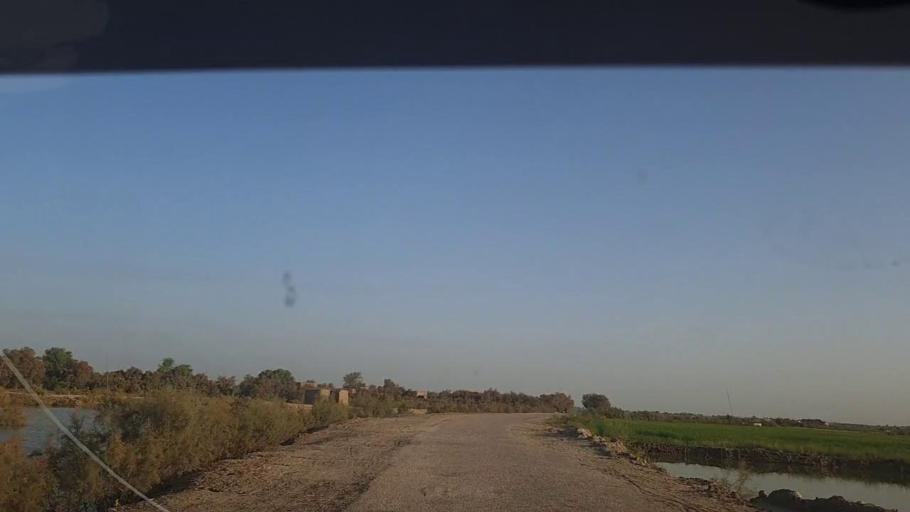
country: PK
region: Sindh
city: Thul
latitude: 28.1479
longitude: 68.8874
